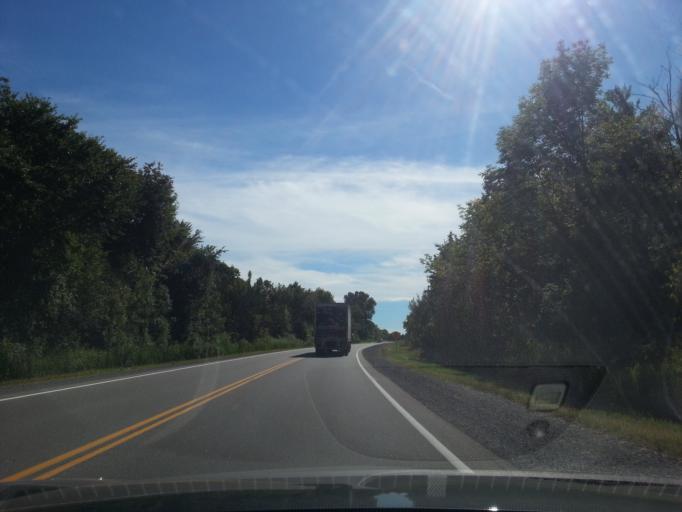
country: CA
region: Ontario
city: Belleville
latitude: 44.1125
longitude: -77.3896
